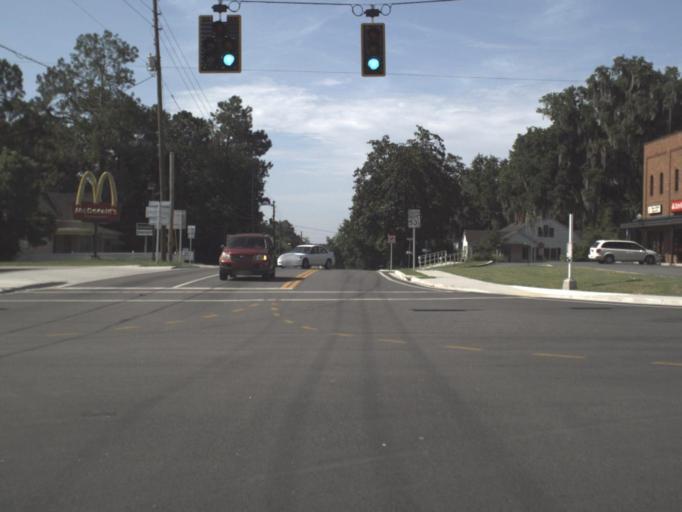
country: US
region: Florida
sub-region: Madison County
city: Madison
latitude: 30.4695
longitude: -83.4101
